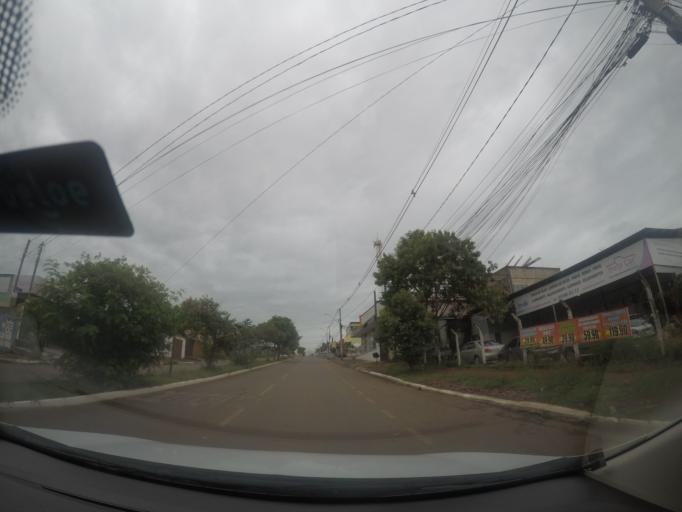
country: BR
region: Goias
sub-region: Goiania
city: Goiania
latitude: -16.6290
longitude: -49.3074
